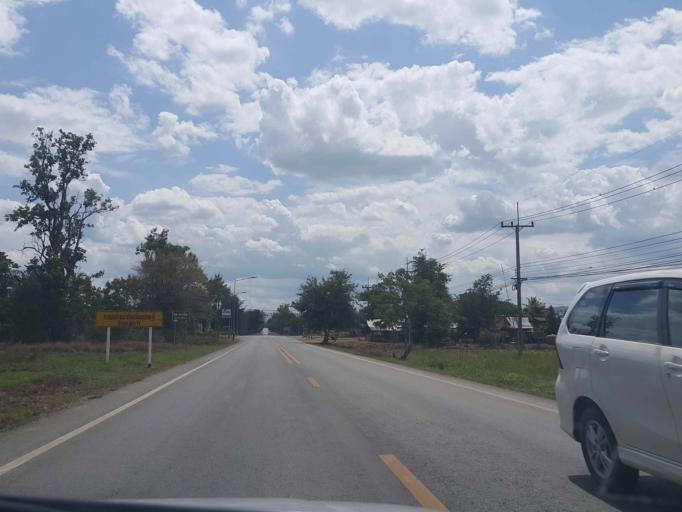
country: TH
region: Sukhothai
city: Thung Saliam
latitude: 17.3355
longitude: 99.5671
